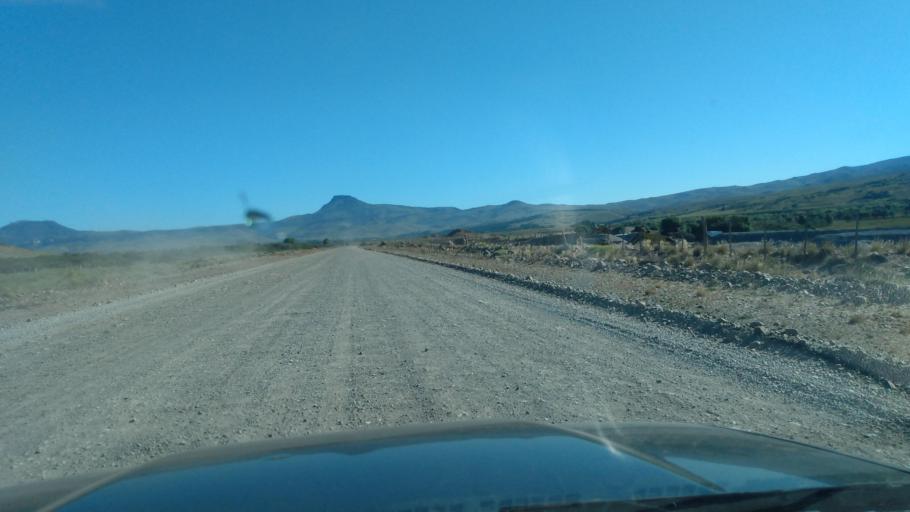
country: AR
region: Neuquen
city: Junin de los Andes
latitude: -39.8556
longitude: -71.1882
